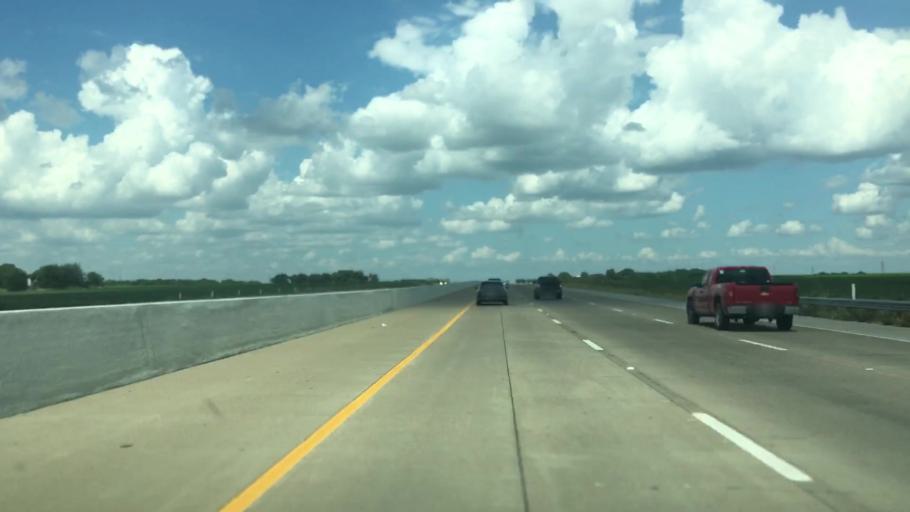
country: US
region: Texas
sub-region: Ellis County
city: Italy
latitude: 32.1512
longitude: -96.9316
